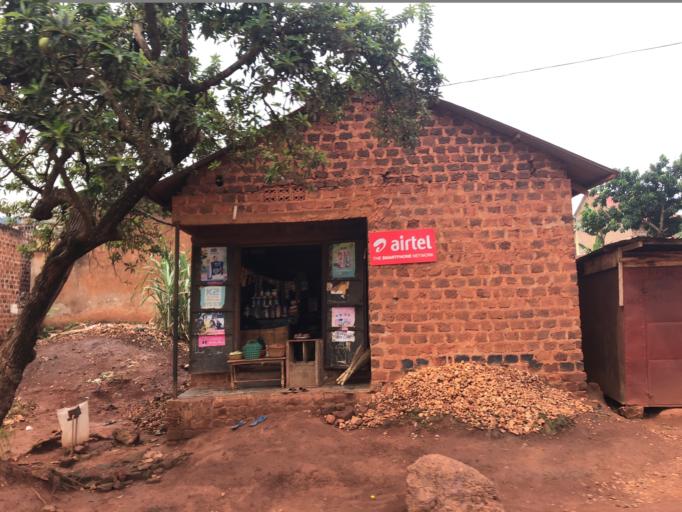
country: UG
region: Central Region
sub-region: Mukono District
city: Mukono
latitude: 0.3522
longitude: 32.7504
